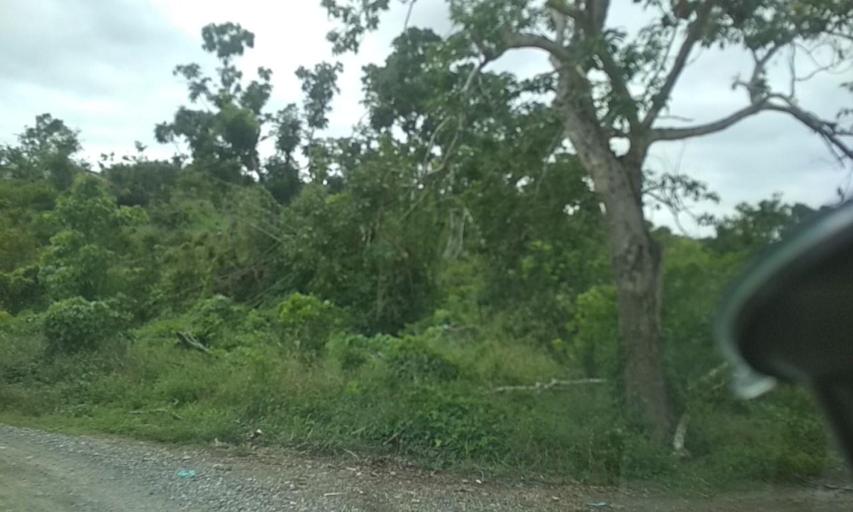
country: MX
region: Veracruz
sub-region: Papantla
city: Polutla
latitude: 20.5831
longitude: -97.2717
